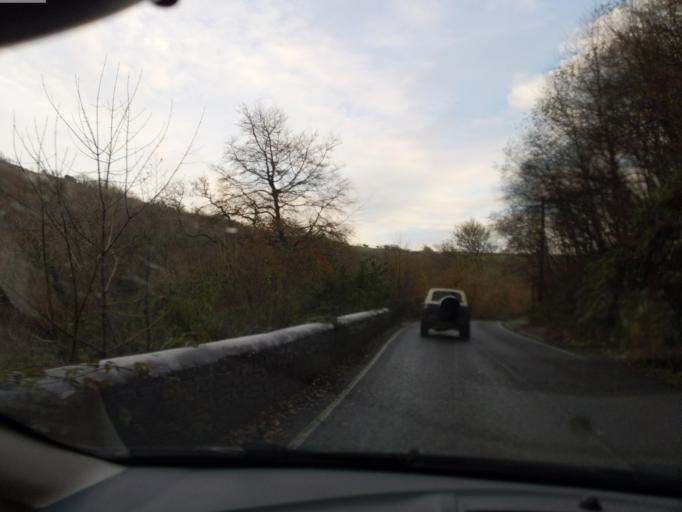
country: GB
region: England
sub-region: Cornwall
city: Looe
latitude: 50.3748
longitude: -4.3918
